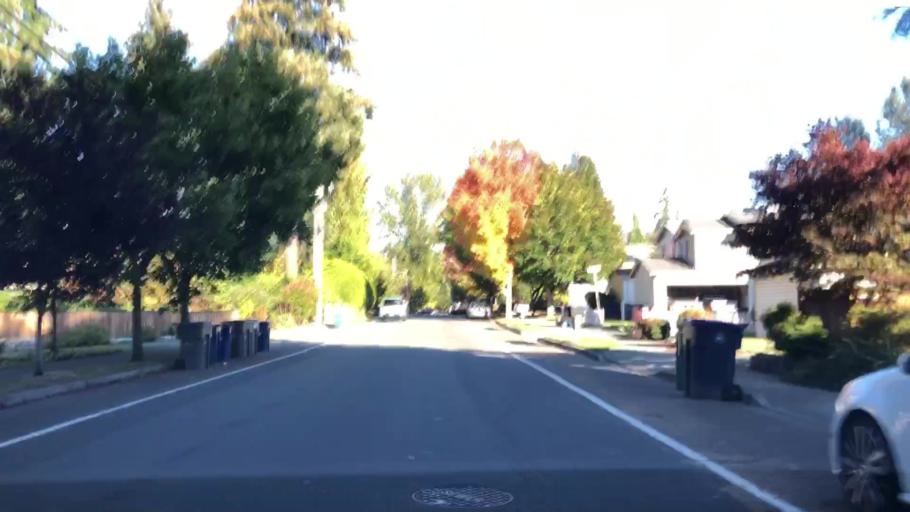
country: US
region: Washington
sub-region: King County
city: Kirkland
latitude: 47.6877
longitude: -122.1786
